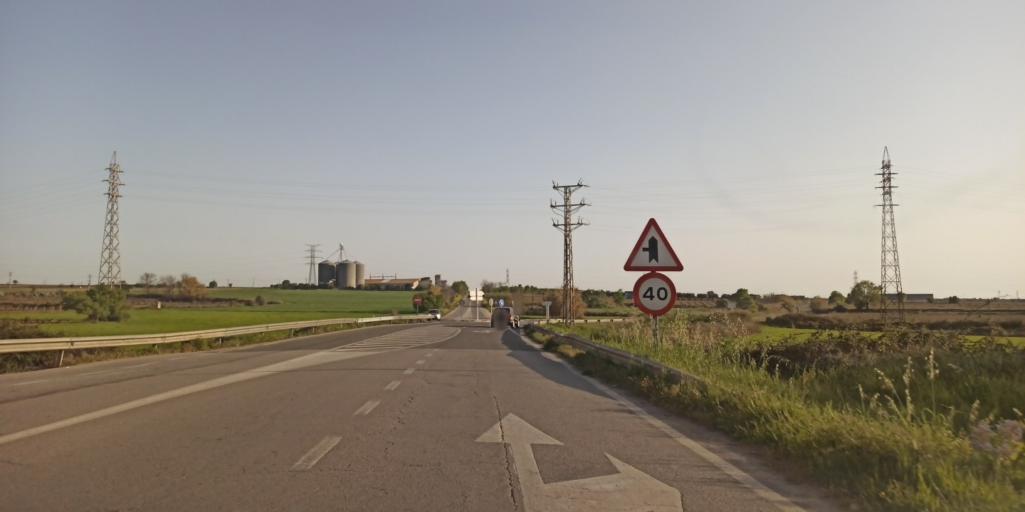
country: ES
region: Catalonia
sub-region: Provincia de Barcelona
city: Vilafranca del Penedes
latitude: 41.3572
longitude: 1.7073
